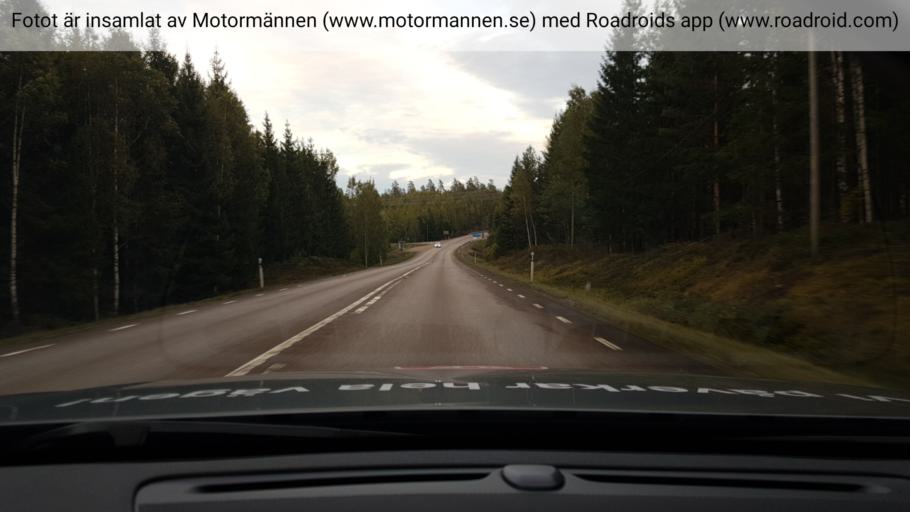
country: SE
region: Vaestra Goetaland
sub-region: Amals Kommun
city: Amal
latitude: 59.0803
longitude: 12.6104
